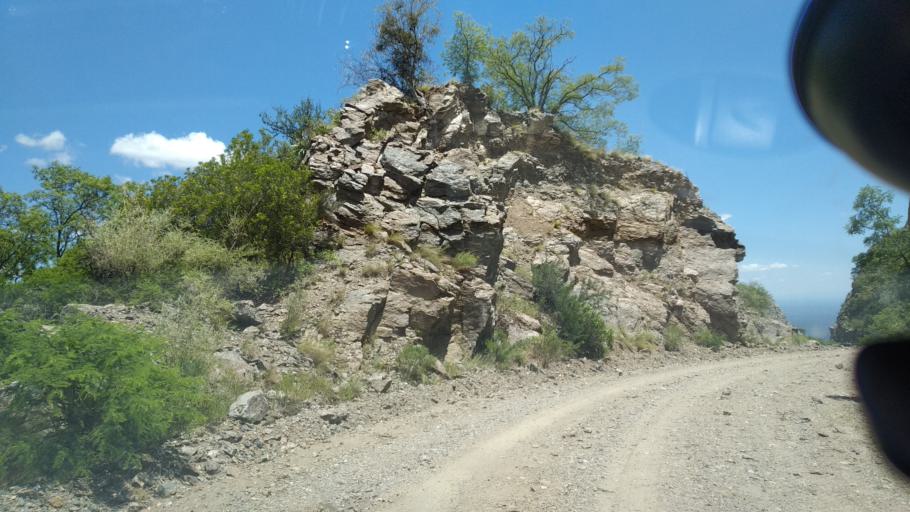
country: AR
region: Cordoba
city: Salsacate
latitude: -31.3708
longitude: -65.4075
